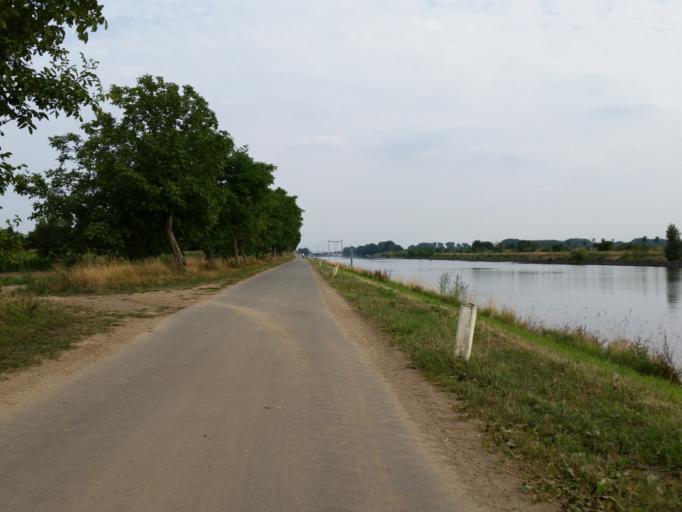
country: BE
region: Flanders
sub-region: Provincie Vlaams-Brabant
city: Grimbergen
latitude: 50.9669
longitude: 4.3999
